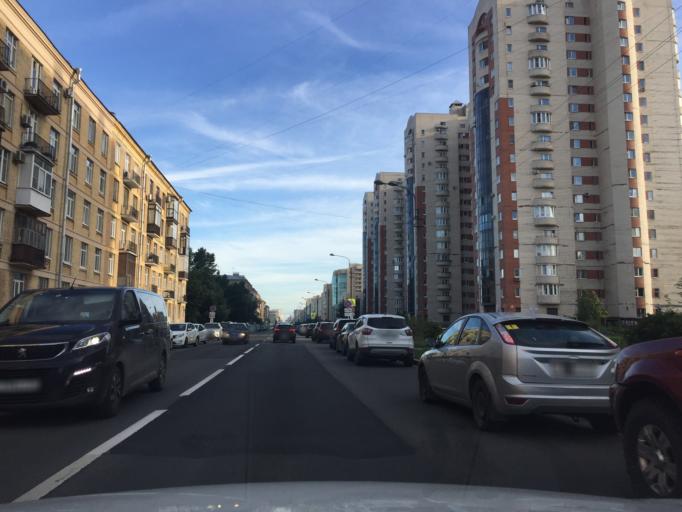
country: RU
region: St.-Petersburg
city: Admiralteisky
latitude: 59.8751
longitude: 30.3134
